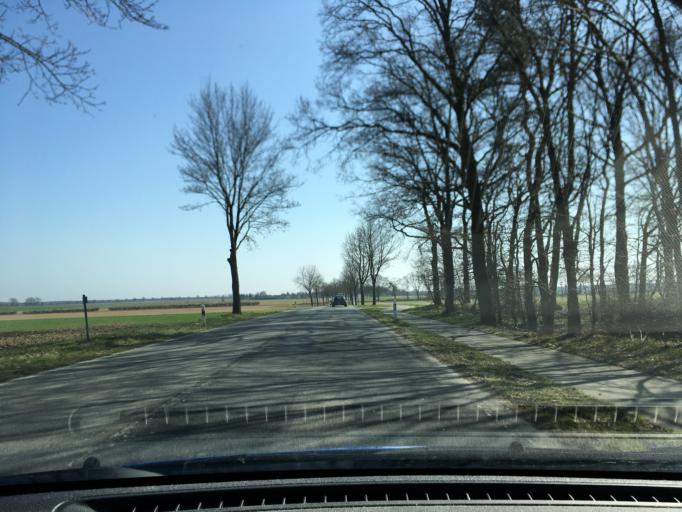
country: DE
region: Lower Saxony
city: Wriedel
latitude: 53.0480
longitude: 10.2934
